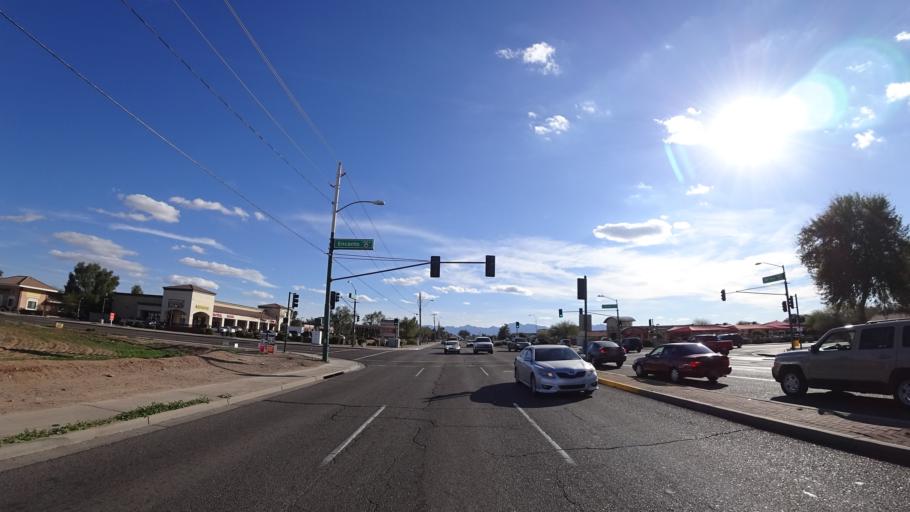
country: US
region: Arizona
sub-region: Maricopa County
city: Tolleson
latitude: 33.4729
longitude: -112.2378
